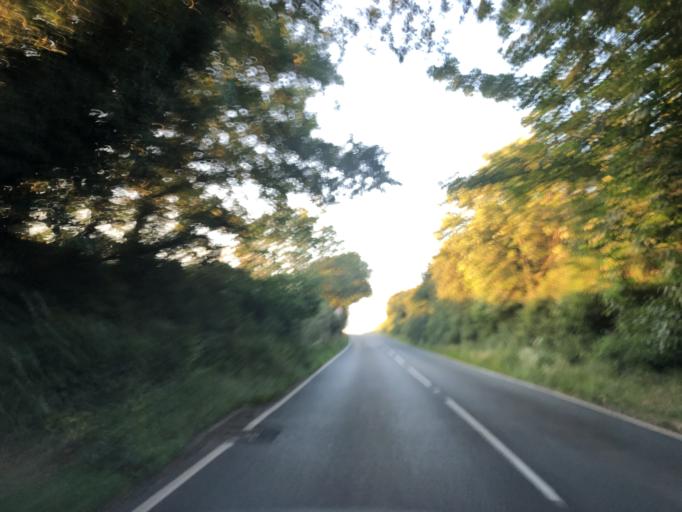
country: GB
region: England
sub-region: Isle of Wight
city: Newport
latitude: 50.6607
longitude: -1.2850
